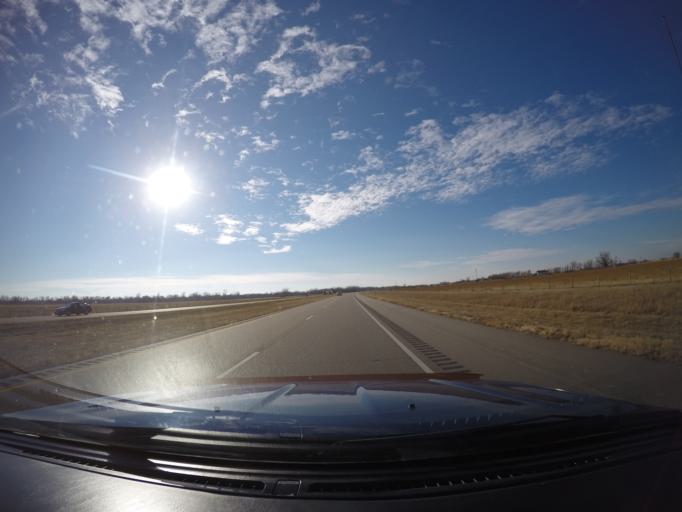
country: US
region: Nebraska
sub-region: Buffalo County
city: Gibbon
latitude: 40.6974
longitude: -98.8612
